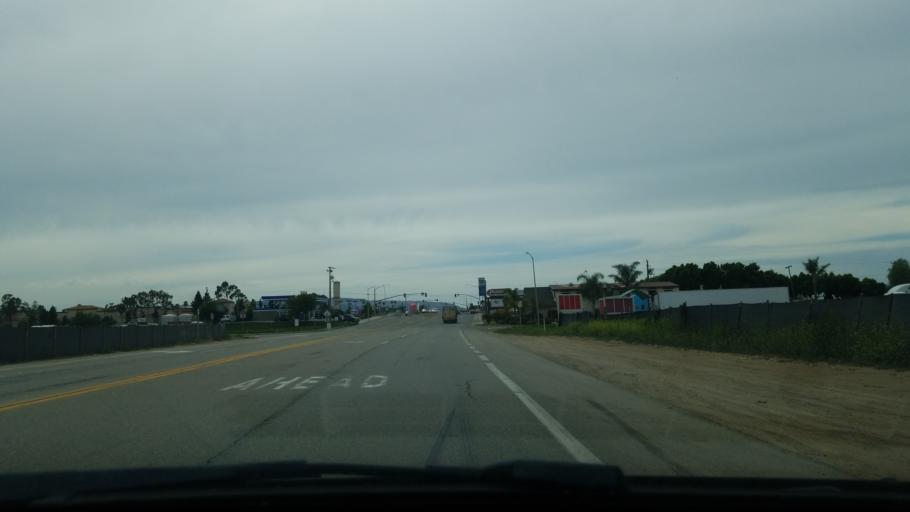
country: US
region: California
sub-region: Santa Barbara County
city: Santa Maria
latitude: 34.9236
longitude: -120.4146
